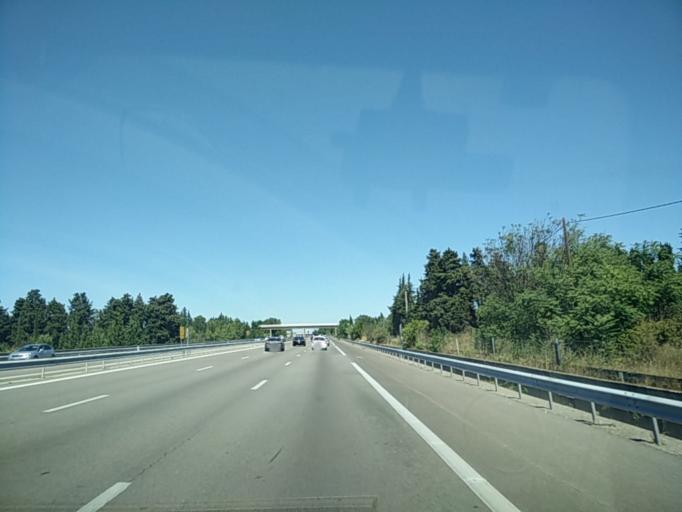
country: FR
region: Provence-Alpes-Cote d'Azur
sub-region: Departement du Vaucluse
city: Morieres-les-Avignon
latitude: 43.9404
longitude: 4.9118
